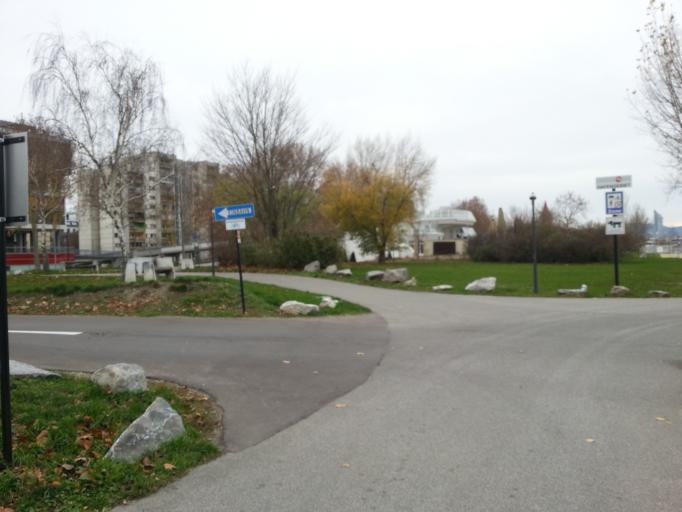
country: AT
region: Vienna
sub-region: Wien Stadt
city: Vienna
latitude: 48.2197
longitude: 16.4144
